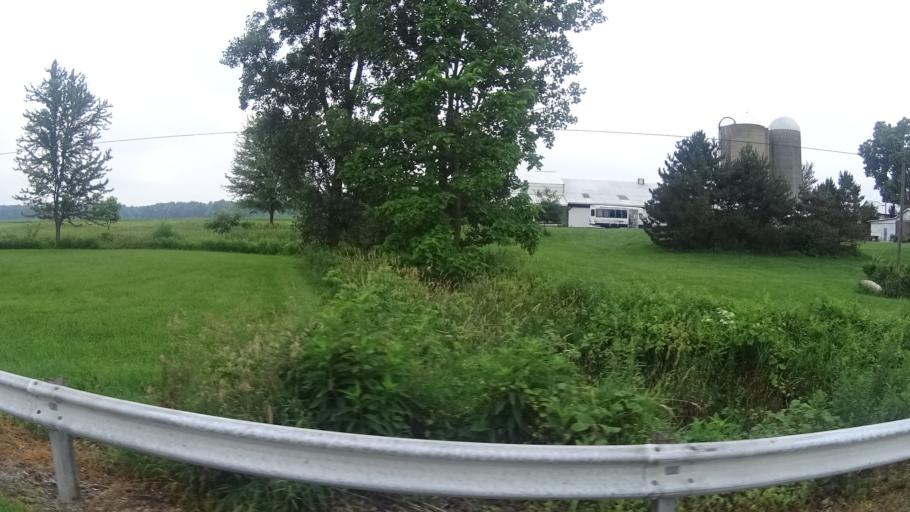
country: US
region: Ohio
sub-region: Erie County
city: Milan
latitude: 41.2954
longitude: -82.5118
